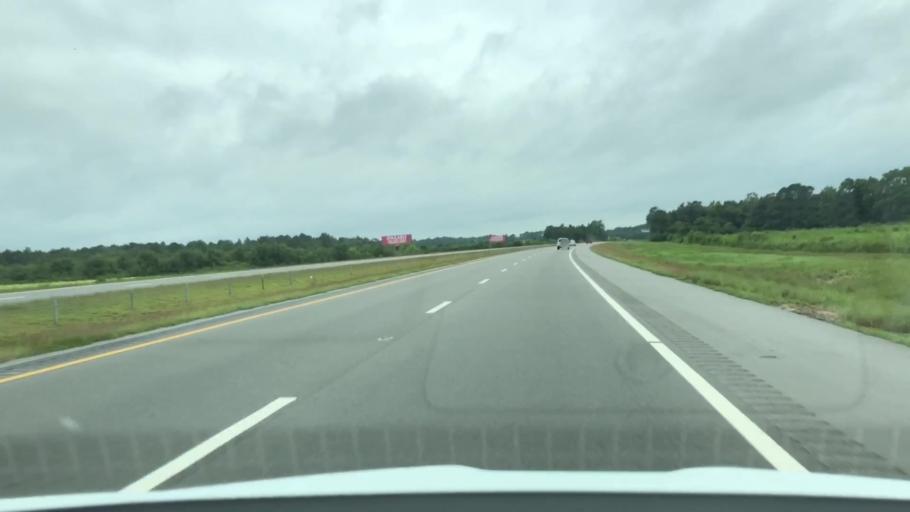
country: US
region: North Carolina
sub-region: Lenoir County
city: La Grange
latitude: 35.3243
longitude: -77.8383
